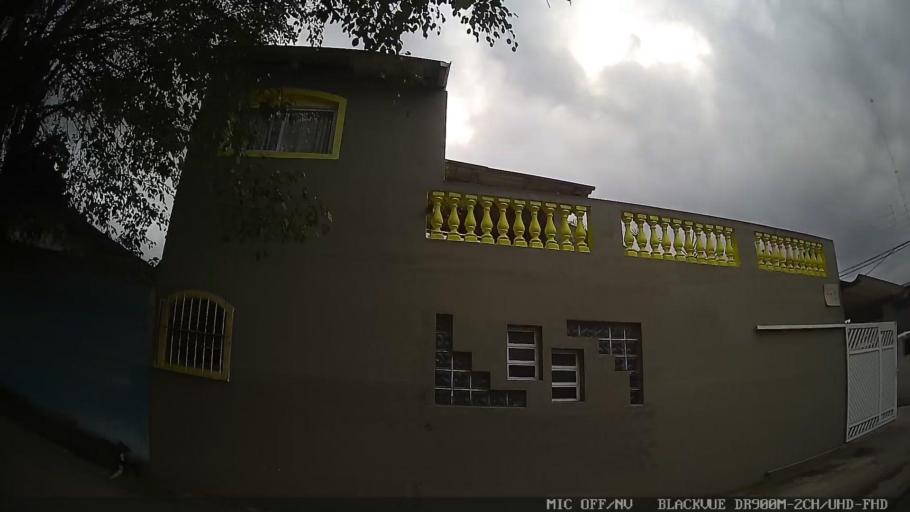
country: BR
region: Sao Paulo
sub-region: Guaruja
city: Guaruja
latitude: -23.9995
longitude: -46.2772
